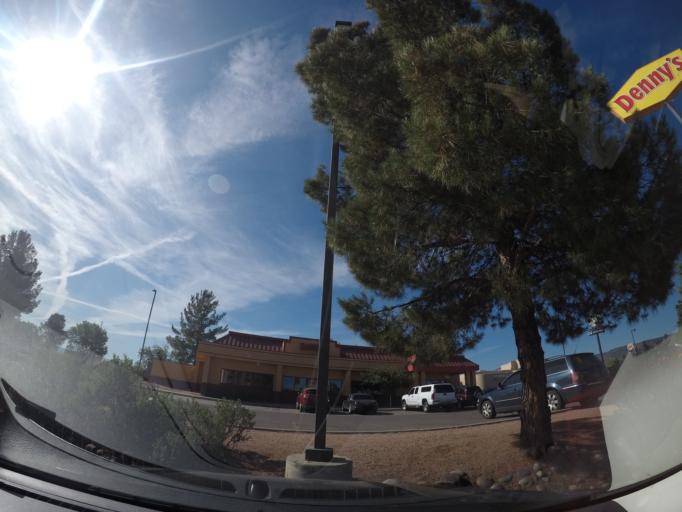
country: US
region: Arizona
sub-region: Yavapai County
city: Camp Verde
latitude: 34.5764
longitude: -111.8817
